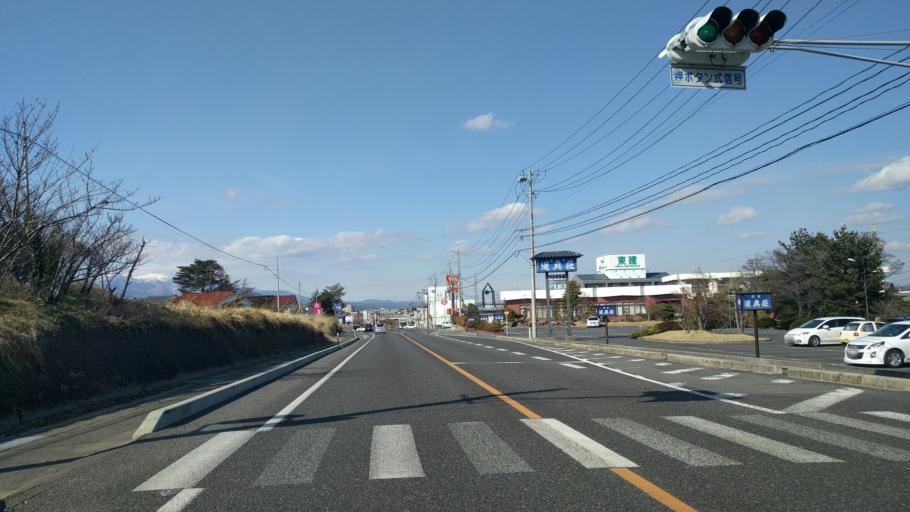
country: JP
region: Fukushima
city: Koriyama
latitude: 37.4394
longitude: 140.3799
